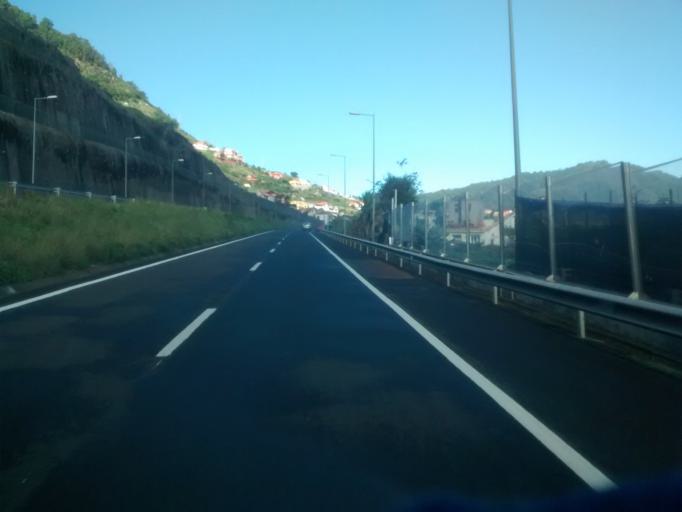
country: PT
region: Madeira
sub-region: Machico
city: Machico
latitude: 32.7191
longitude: -16.7725
